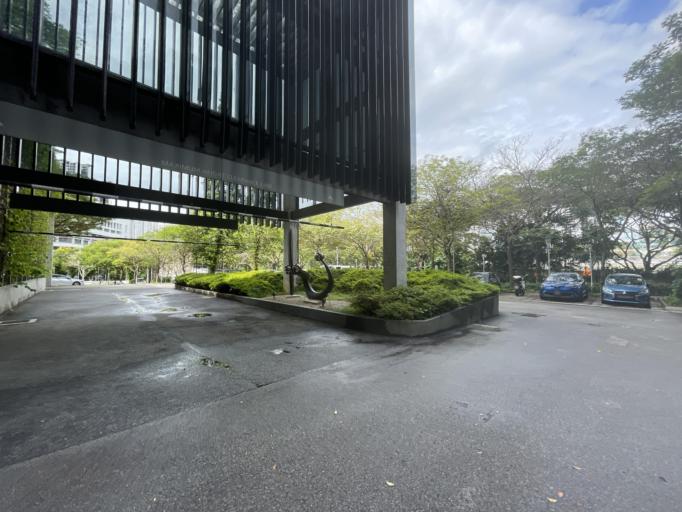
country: SG
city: Singapore
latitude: 1.3029
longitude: 103.7704
